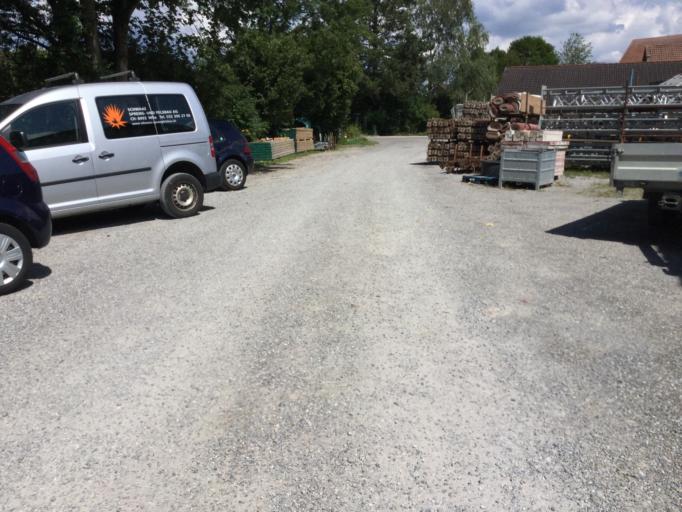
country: CH
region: Zurich
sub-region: Bezirk Pfaeffikon
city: Fehraltorf
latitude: 47.3833
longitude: 8.7547
